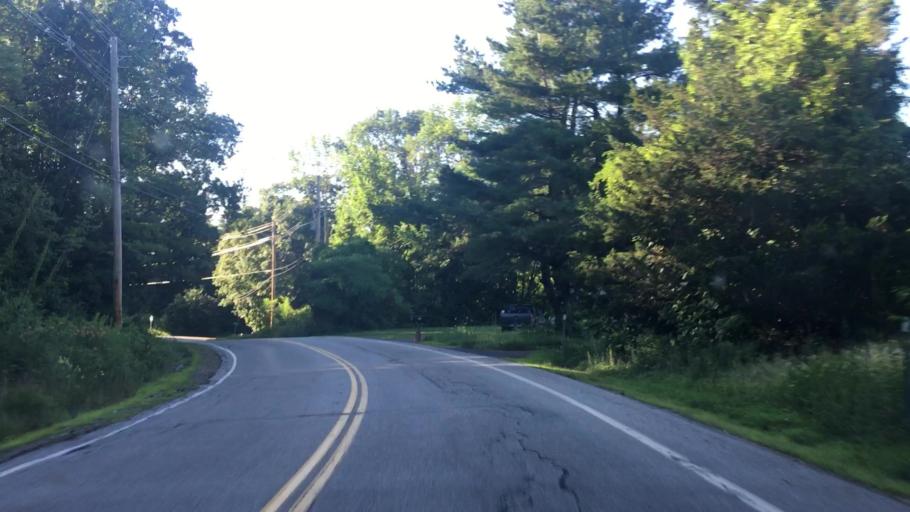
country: US
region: New Hampshire
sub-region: Rockingham County
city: Sandown
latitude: 42.9560
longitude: -71.1987
